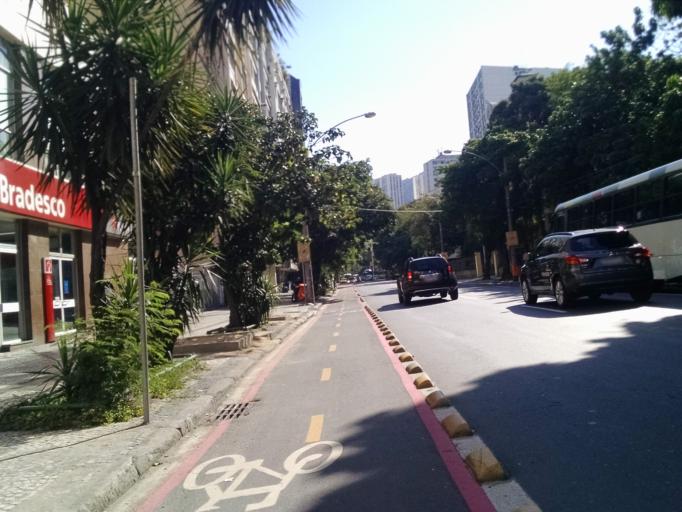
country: BR
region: Rio de Janeiro
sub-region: Rio De Janeiro
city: Rio de Janeiro
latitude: -22.9339
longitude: -43.1864
